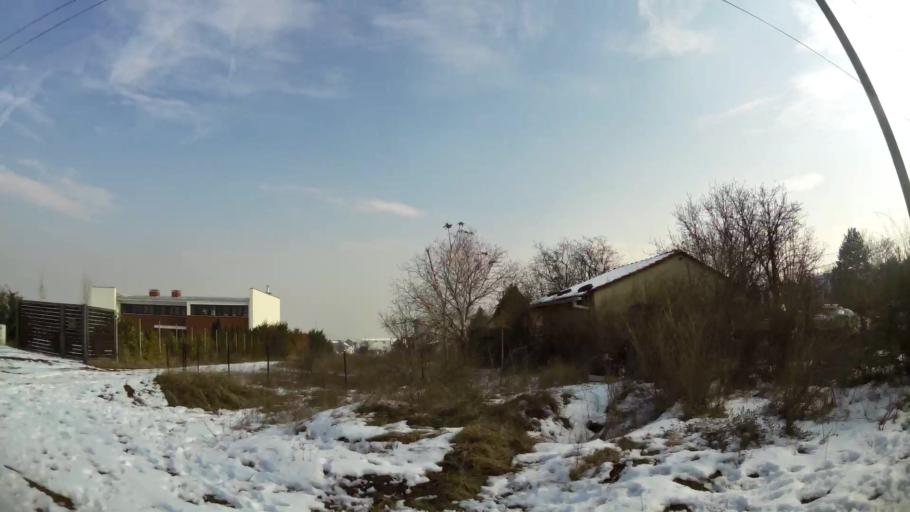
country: MK
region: Suto Orizari
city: Suto Orizare
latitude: 42.0323
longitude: 21.3772
